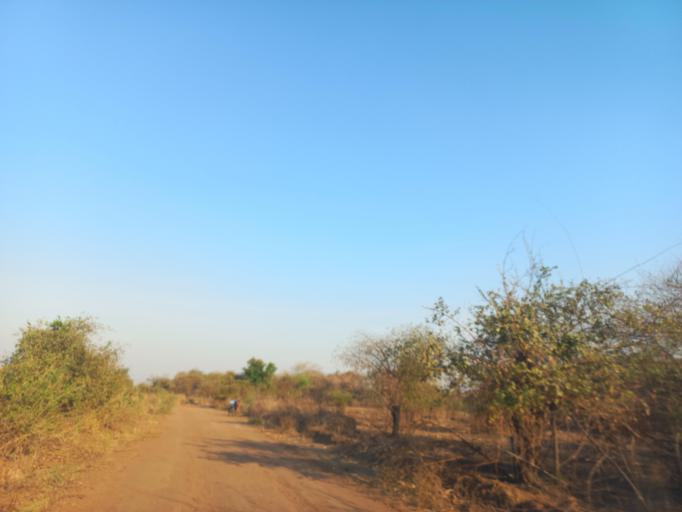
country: ZM
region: Lusaka
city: Luangwa
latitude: -15.4301
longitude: 30.3408
